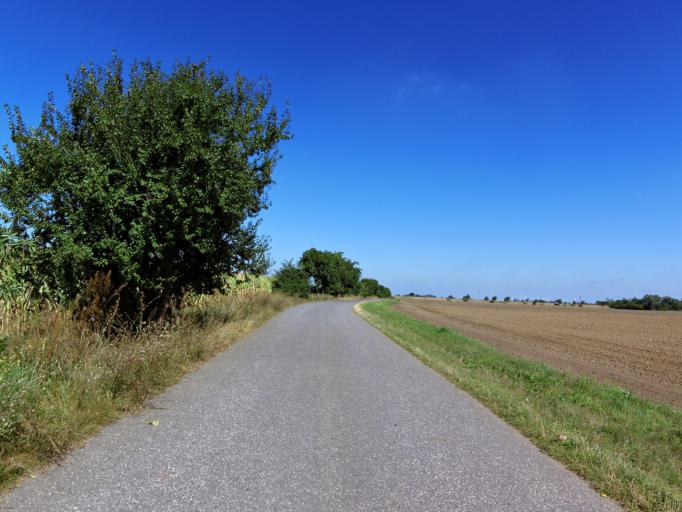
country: DE
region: Brandenburg
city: Muhlberg
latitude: 51.3998
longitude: 13.2440
